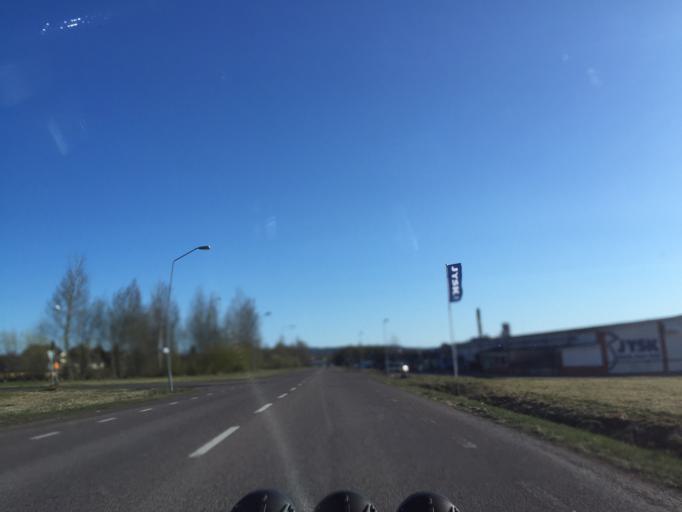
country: SE
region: Dalarna
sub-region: Borlange Kommun
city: Borlaenge
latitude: 60.4705
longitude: 15.3987
